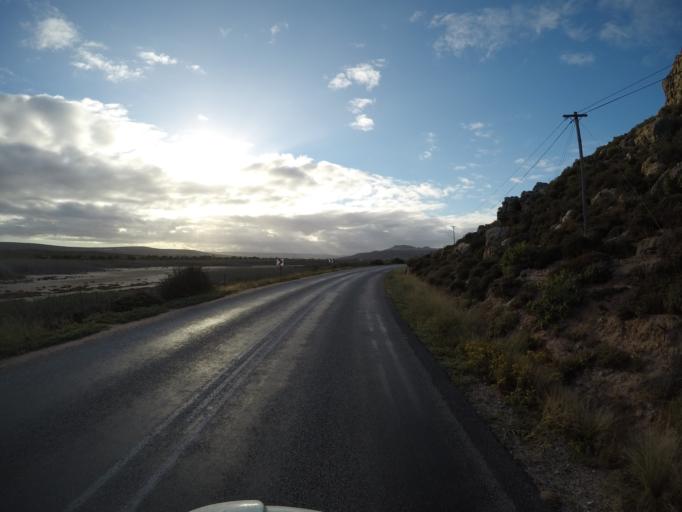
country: ZA
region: Western Cape
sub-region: West Coast District Municipality
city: Clanwilliam
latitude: -32.3156
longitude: 18.3562
